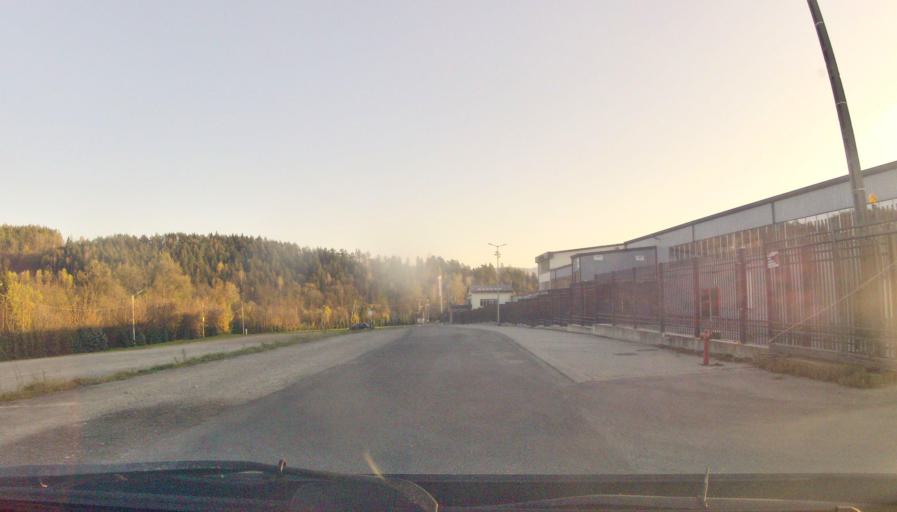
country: PL
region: Lesser Poland Voivodeship
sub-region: Powiat suski
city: Kukow
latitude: 49.7482
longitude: 19.4652
